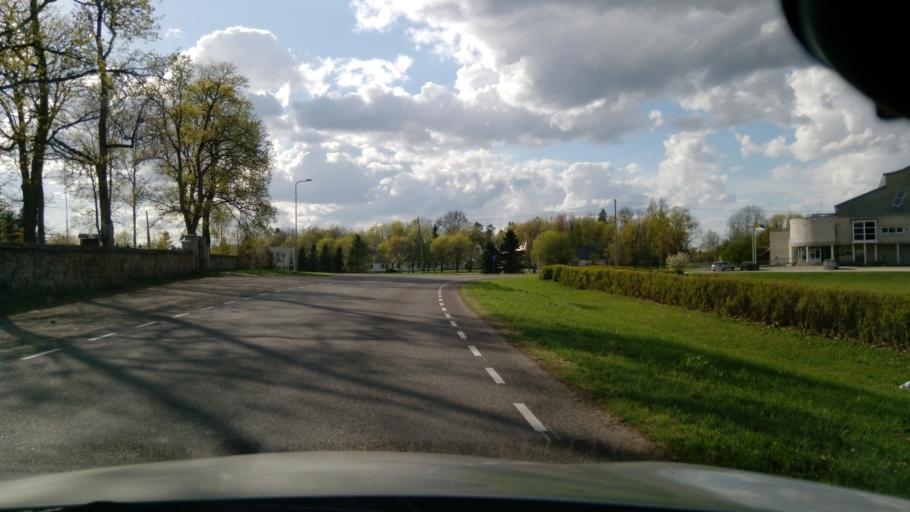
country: EE
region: Jaervamaa
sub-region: Jaerva-Jaani vald
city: Jarva-Jaani
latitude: 58.9429
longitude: 25.8366
